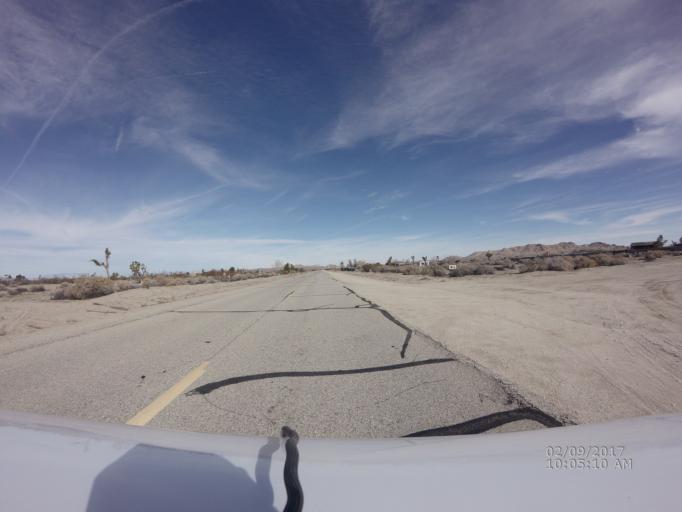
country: US
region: California
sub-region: Los Angeles County
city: Lake Los Angeles
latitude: 34.5672
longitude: -117.8896
